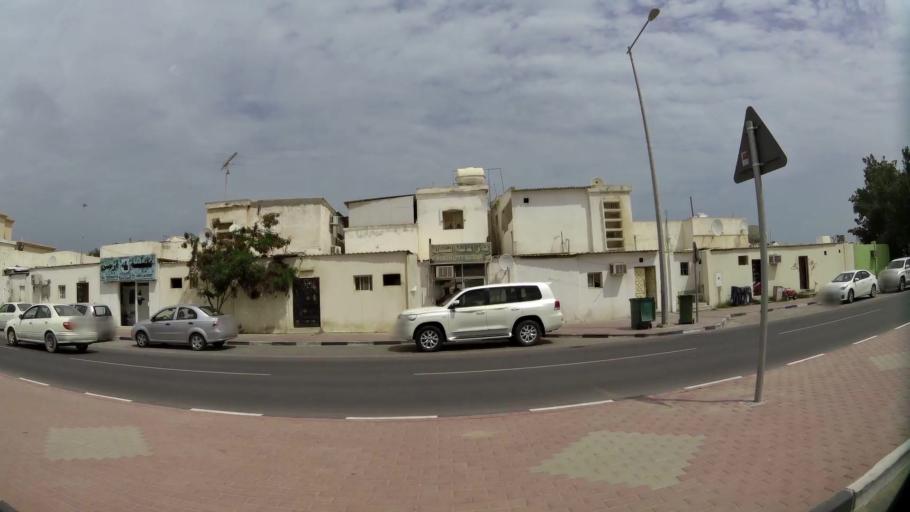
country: QA
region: Baladiyat ar Rayyan
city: Ar Rayyan
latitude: 25.3275
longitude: 51.4717
